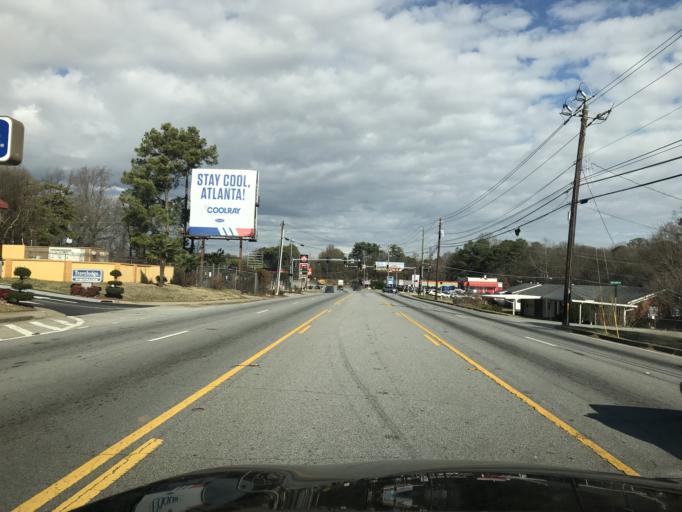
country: US
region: Georgia
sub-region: Clayton County
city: Forest Park
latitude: 33.5898
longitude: -84.3774
